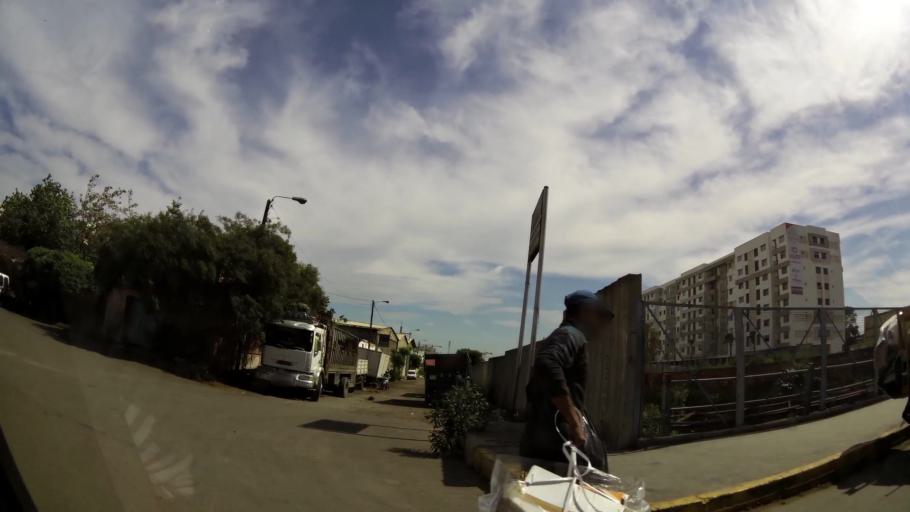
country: MA
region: Grand Casablanca
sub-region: Casablanca
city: Casablanca
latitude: 33.5841
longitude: -7.5966
